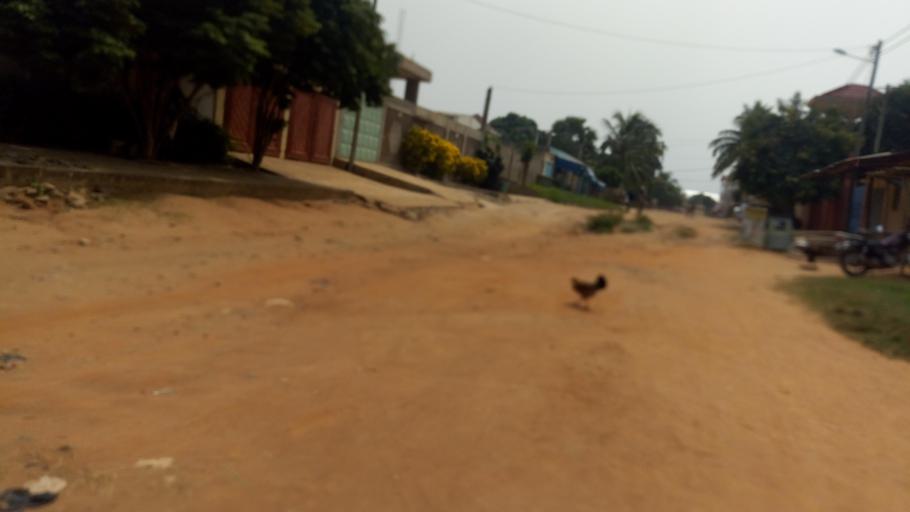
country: TG
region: Maritime
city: Lome
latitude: 6.1761
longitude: 1.1746
